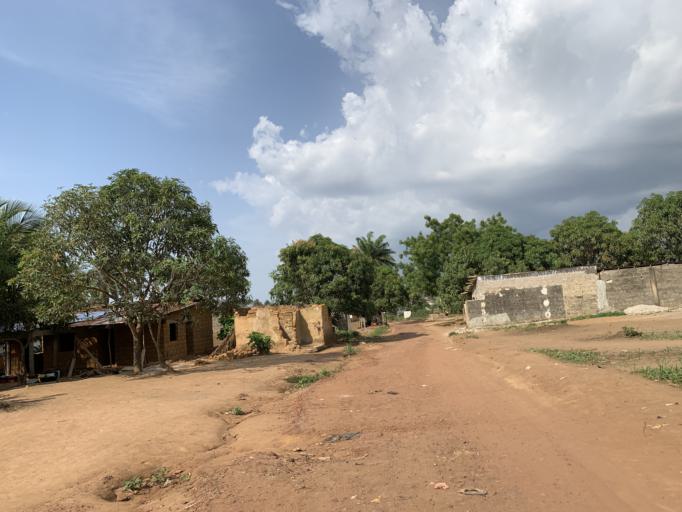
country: SL
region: Western Area
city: Waterloo
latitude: 8.3436
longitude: -13.0476
